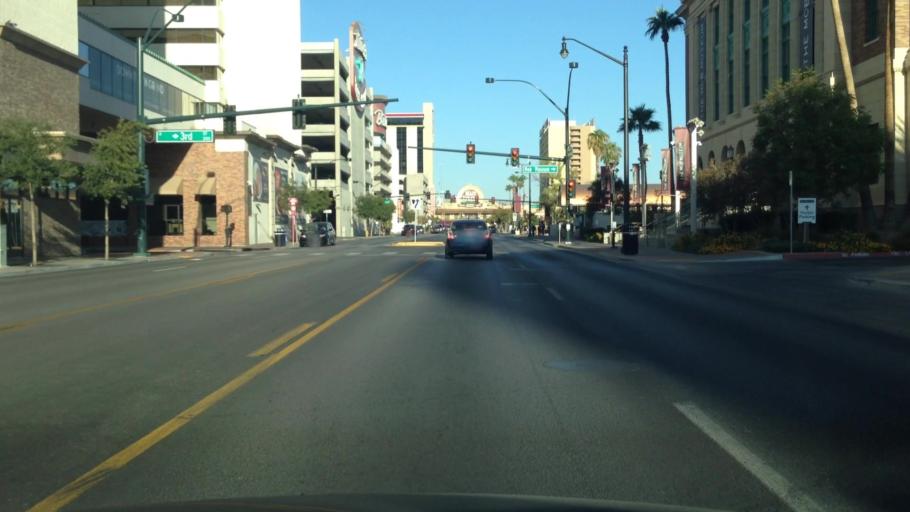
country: US
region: Nevada
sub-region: Clark County
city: Las Vegas
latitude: 36.1723
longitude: -115.1408
